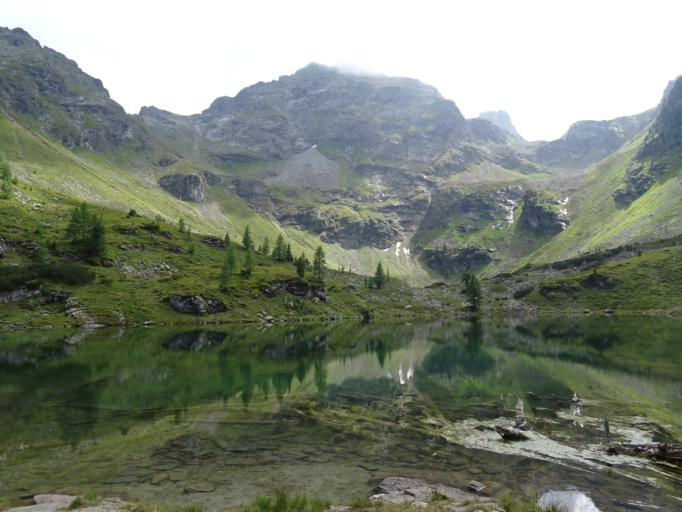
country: AT
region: Styria
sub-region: Politischer Bezirk Liezen
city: Haus
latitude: 47.3589
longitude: 13.7923
